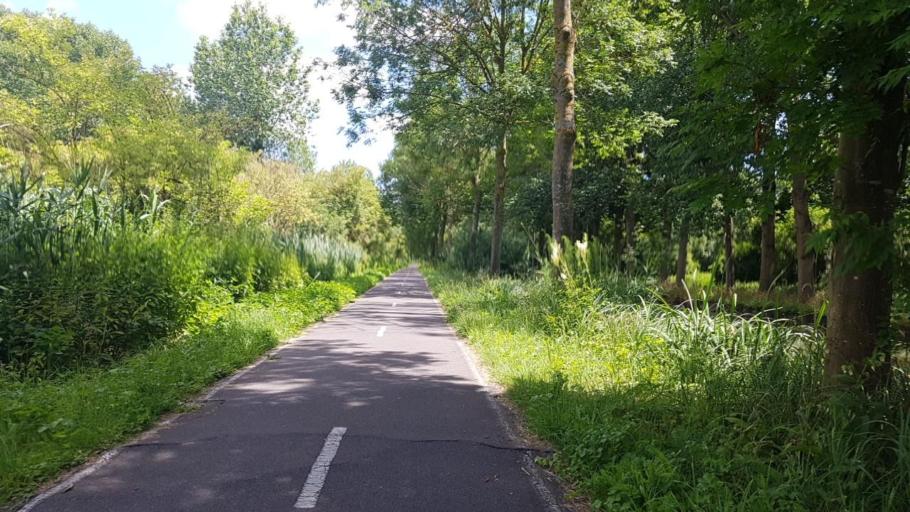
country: FR
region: Ile-de-France
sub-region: Departement de Seine-et-Marne
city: Villeparisis
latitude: 48.9542
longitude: 2.6394
